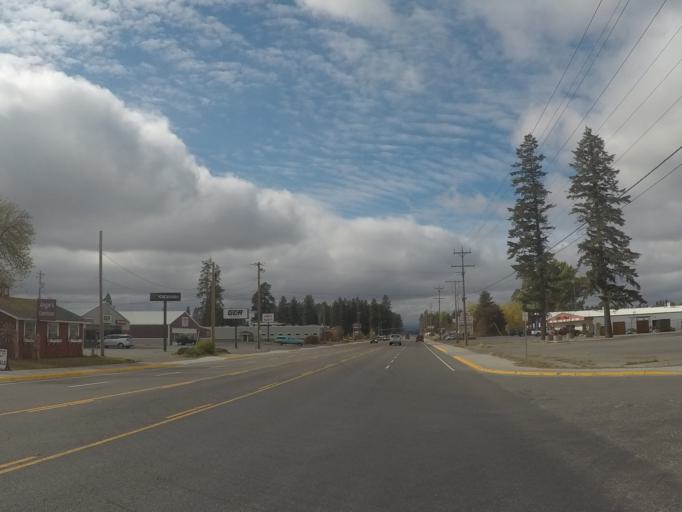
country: US
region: Montana
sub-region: Flathead County
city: Columbia Falls
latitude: 48.3707
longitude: -114.2047
